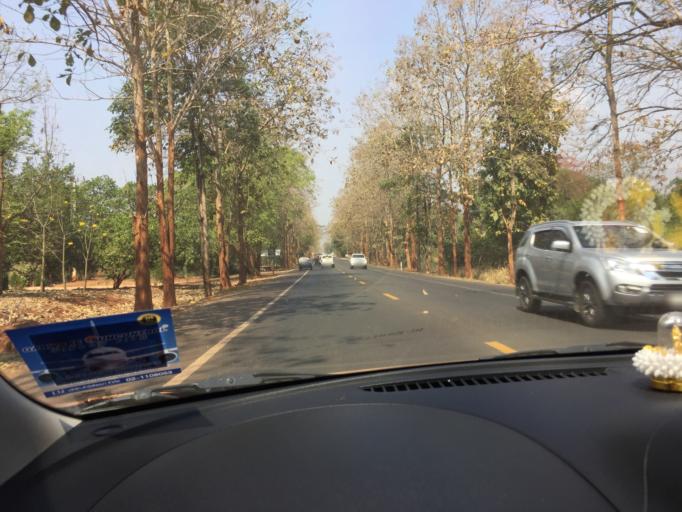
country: TH
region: Kanchanaburi
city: Sai Yok
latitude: 14.1693
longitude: 99.1318
